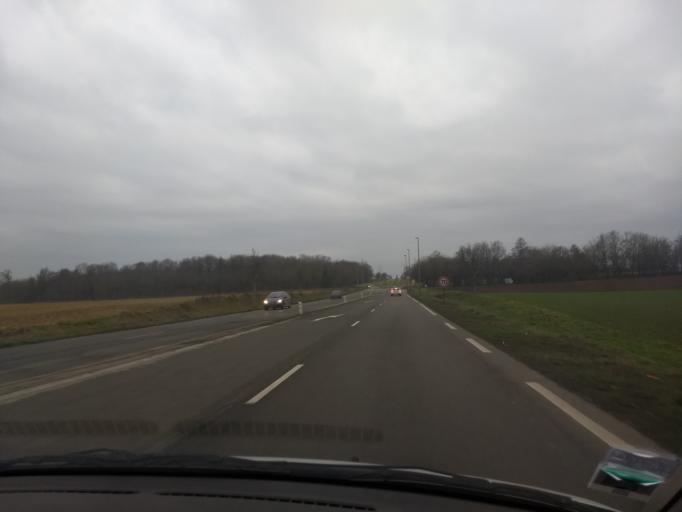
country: FR
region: Nord-Pas-de-Calais
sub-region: Departement du Pas-de-Calais
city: Tilloy-les-Mofflaines
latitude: 50.2752
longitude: 2.8338
